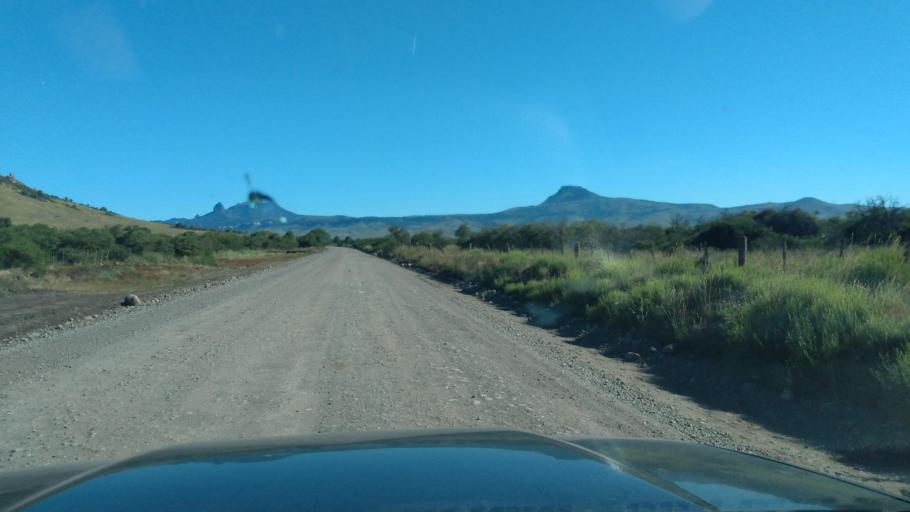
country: AR
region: Neuquen
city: Junin de los Andes
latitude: -39.8438
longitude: -71.1885
